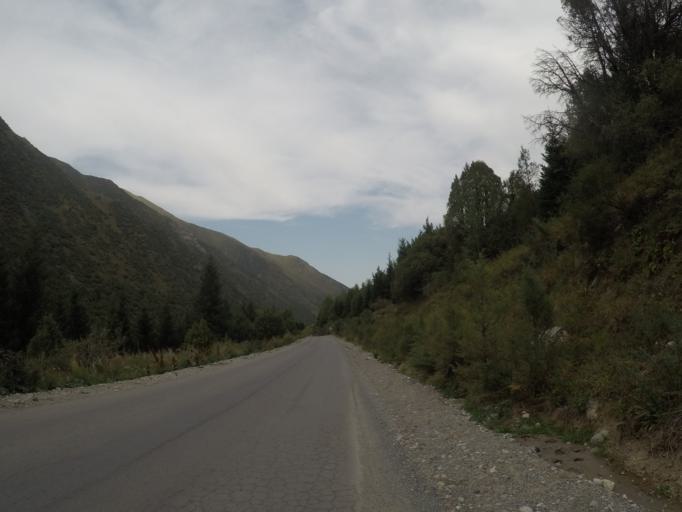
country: KG
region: Chuy
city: Bishkek
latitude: 42.5884
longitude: 74.4840
